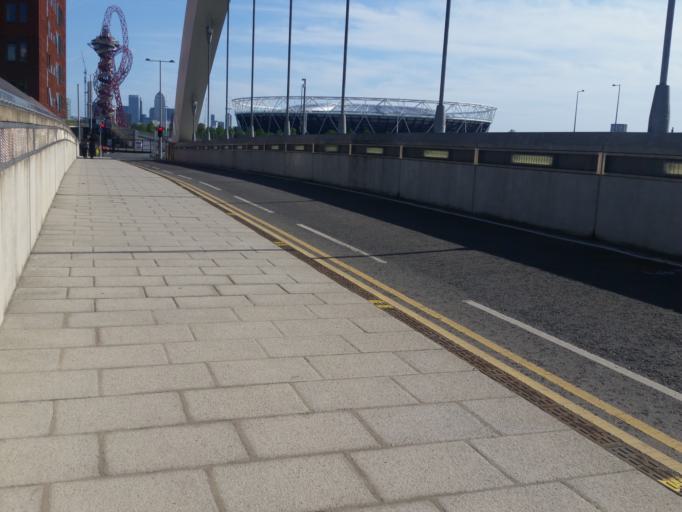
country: GB
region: England
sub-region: Greater London
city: Poplar
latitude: 51.5451
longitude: -0.0125
